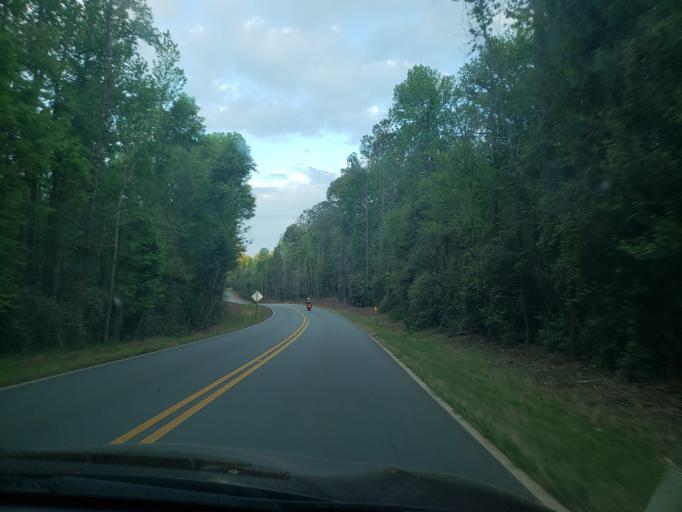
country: US
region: Alabama
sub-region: Tallapoosa County
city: Dadeville
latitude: 32.7106
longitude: -85.7767
